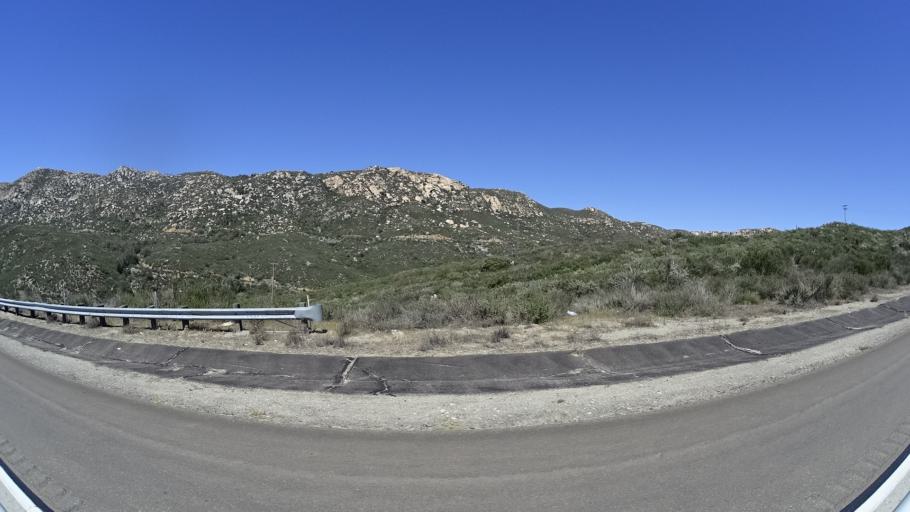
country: US
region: California
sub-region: San Diego County
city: Descanso
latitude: 32.8357
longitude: -116.6386
